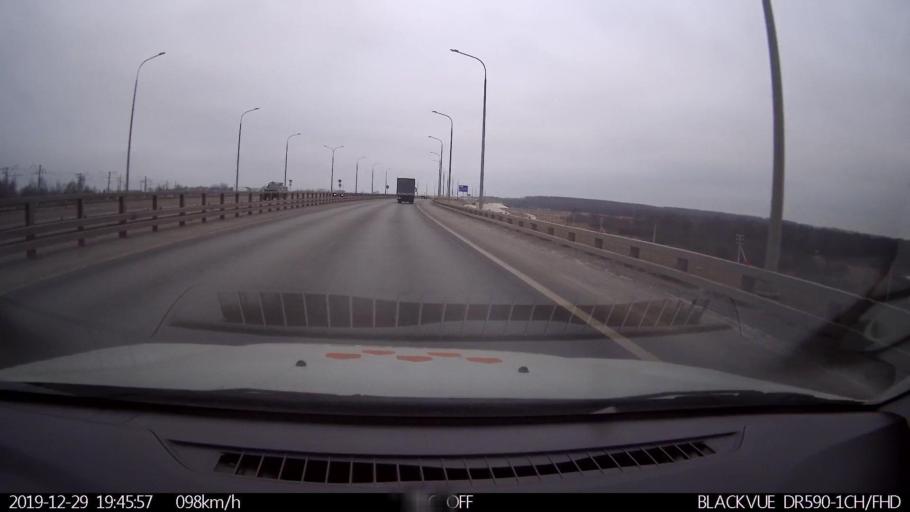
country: RU
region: Nizjnij Novgorod
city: Neklyudovo
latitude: 56.3896
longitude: 43.9731
